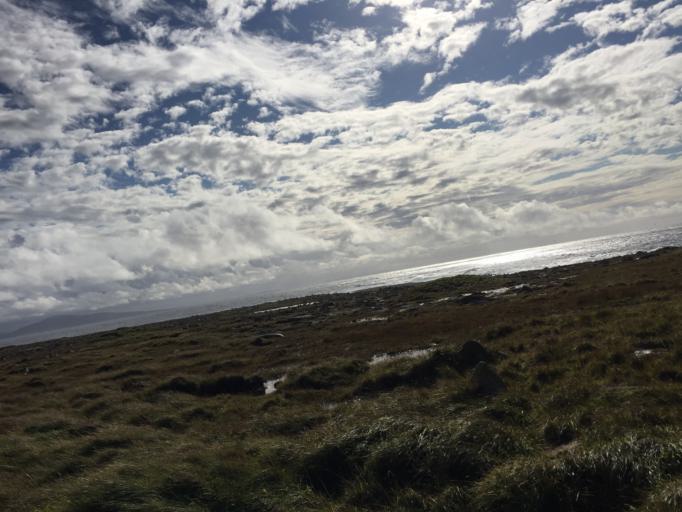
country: IE
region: Ulster
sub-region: County Donegal
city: Derrybeg
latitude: 55.2712
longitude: -8.2488
